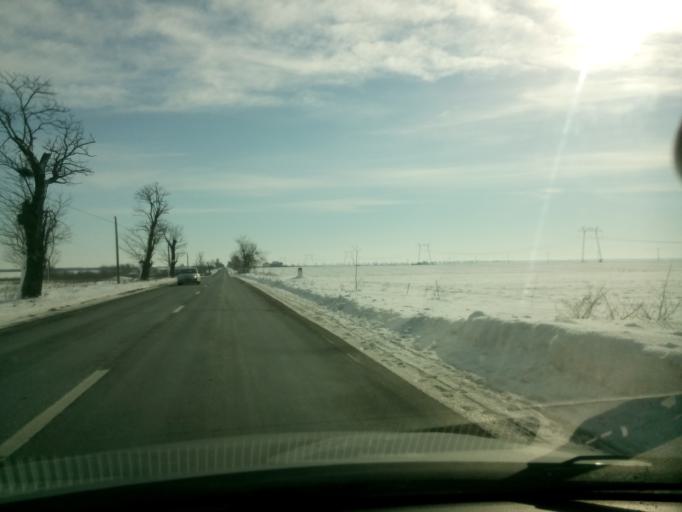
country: RO
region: Calarasi
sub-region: Comuna Frumusani
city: Frumusani
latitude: 44.2691
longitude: 26.3465
